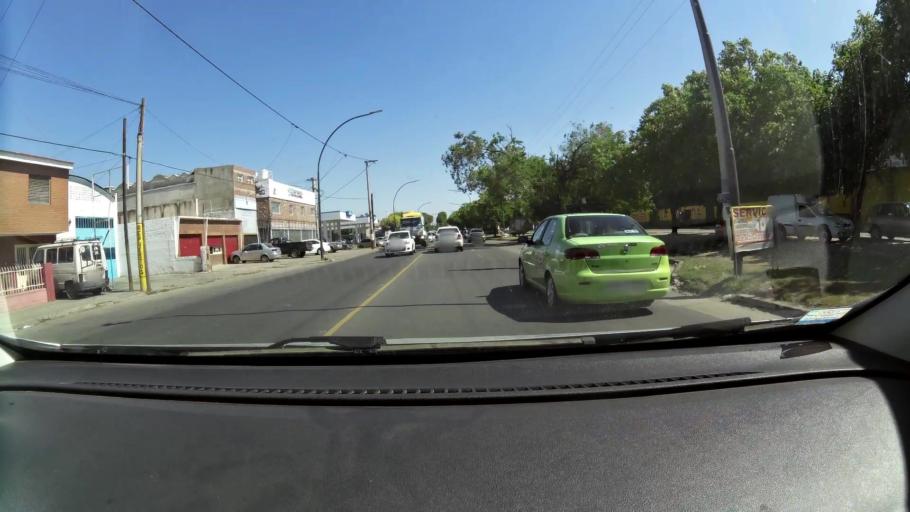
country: AR
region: Cordoba
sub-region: Departamento de Capital
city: Cordoba
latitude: -31.3703
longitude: -64.1763
